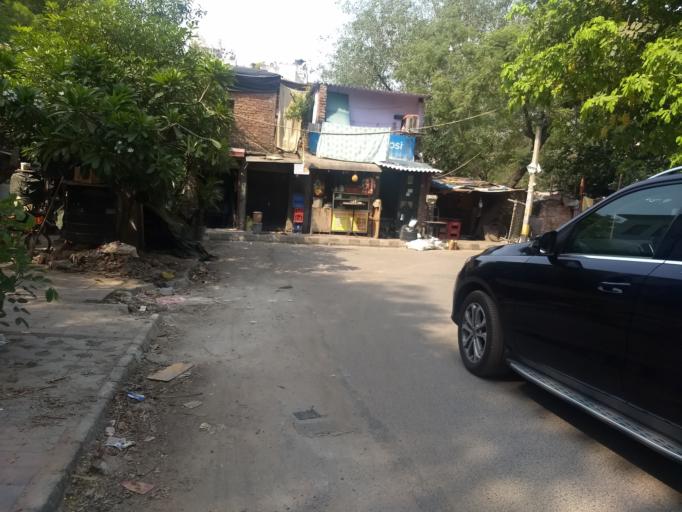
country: IN
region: NCT
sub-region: New Delhi
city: New Delhi
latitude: 28.5653
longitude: 77.2233
